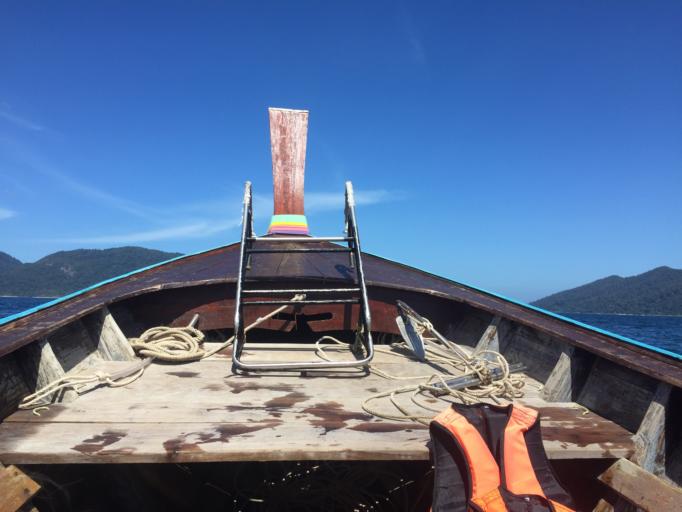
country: MY
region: Kedah
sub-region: Langkawi
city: Kuah
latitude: 6.5180
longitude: 99.2622
